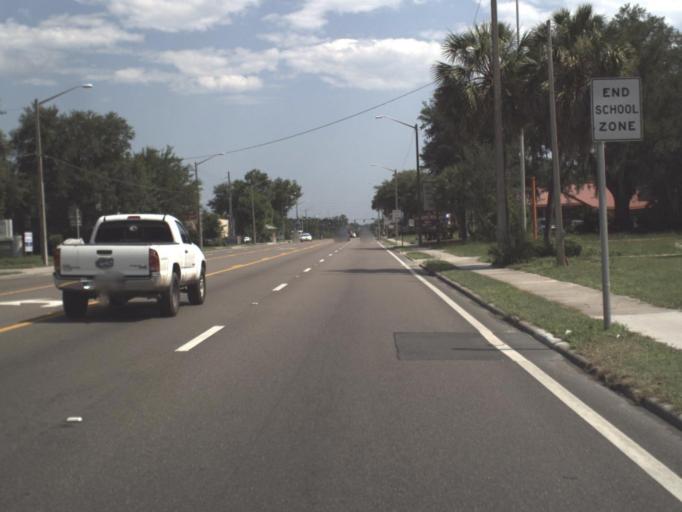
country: US
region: Florida
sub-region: Alachua County
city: Gainesville
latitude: 29.6708
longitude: -82.3391
